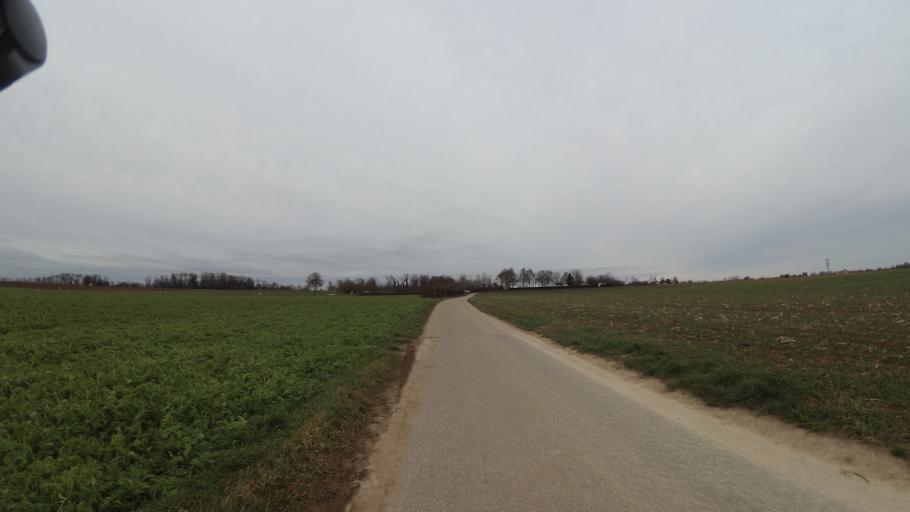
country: DE
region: Baden-Wuerttemberg
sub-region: Regierungsbezirk Stuttgart
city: Oedheim
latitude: 49.2299
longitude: 9.2484
